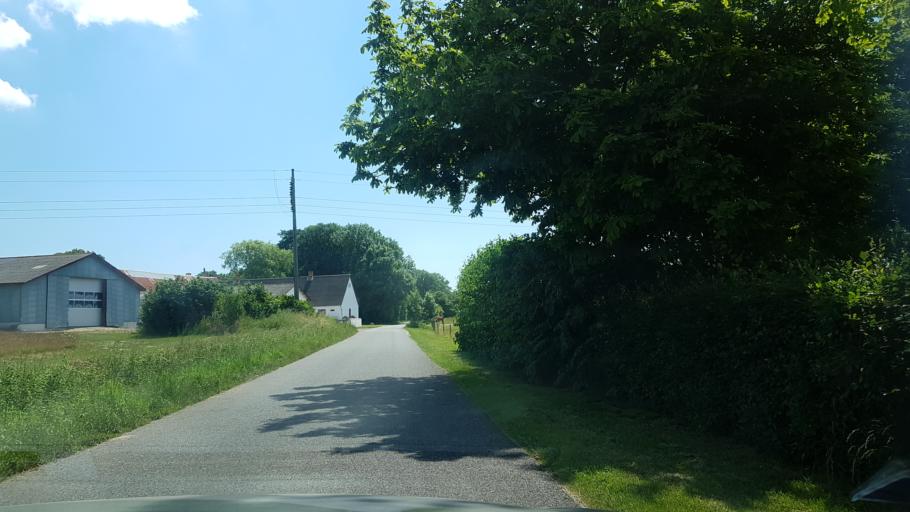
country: DK
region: Zealand
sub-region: Kalundborg Kommune
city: Svebolle
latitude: 55.7014
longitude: 11.2926
